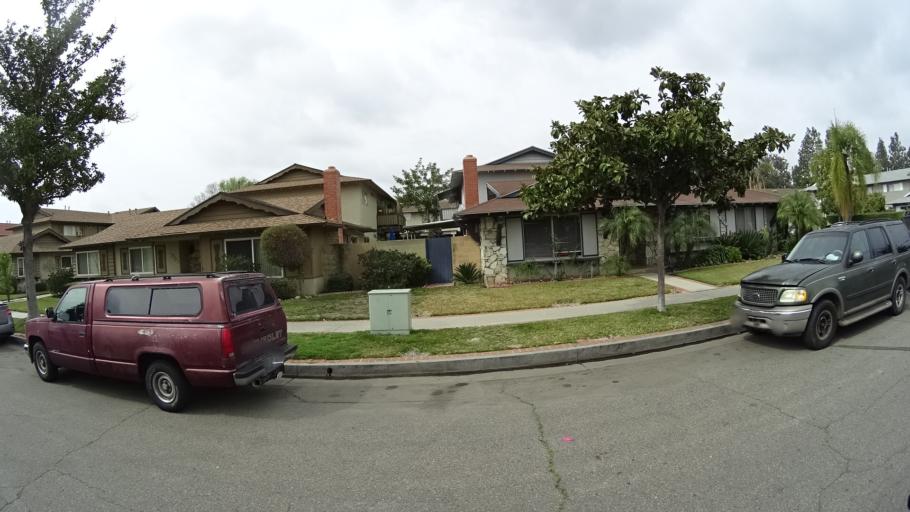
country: US
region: California
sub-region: Orange County
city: Stanton
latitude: 33.8294
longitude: -117.9962
